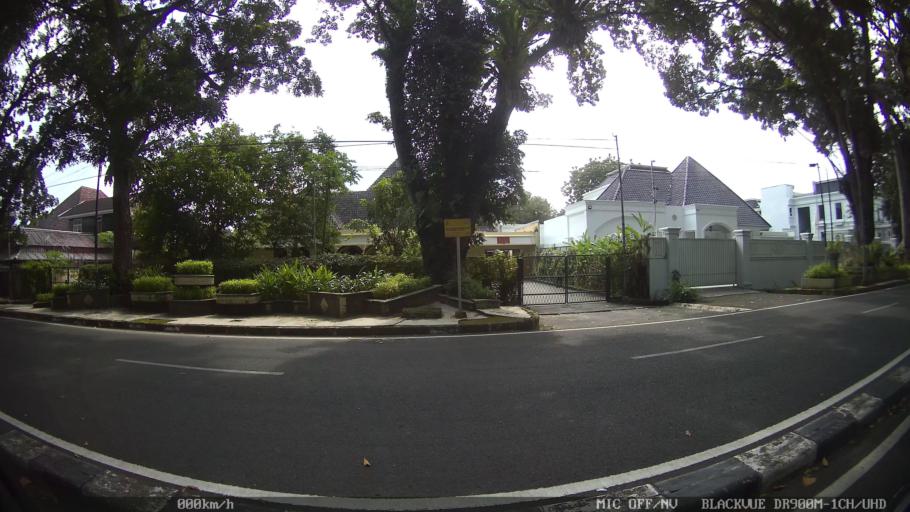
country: ID
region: North Sumatra
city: Medan
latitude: 3.5730
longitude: 98.6778
